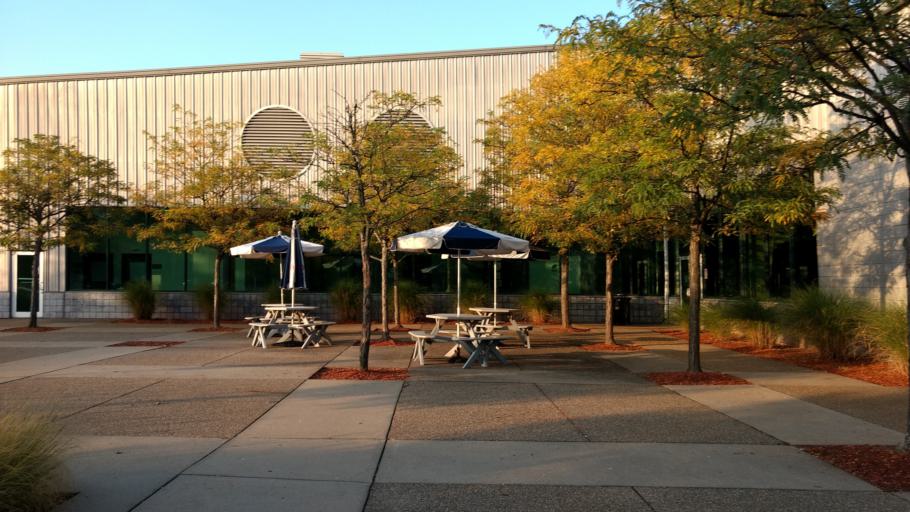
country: US
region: Pennsylvania
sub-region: Allegheny County
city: Coraopolis
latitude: 40.5185
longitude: -80.1508
